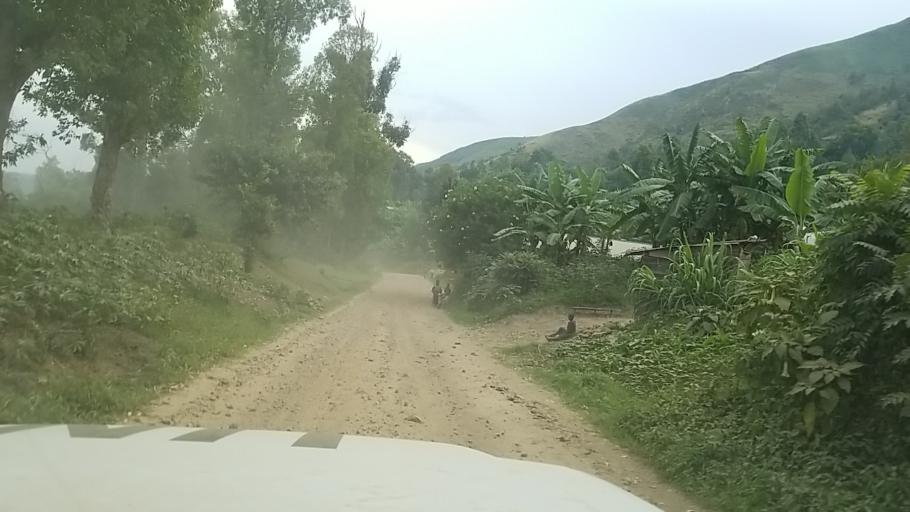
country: RW
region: Western Province
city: Cyangugu
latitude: -2.1332
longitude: 28.8611
